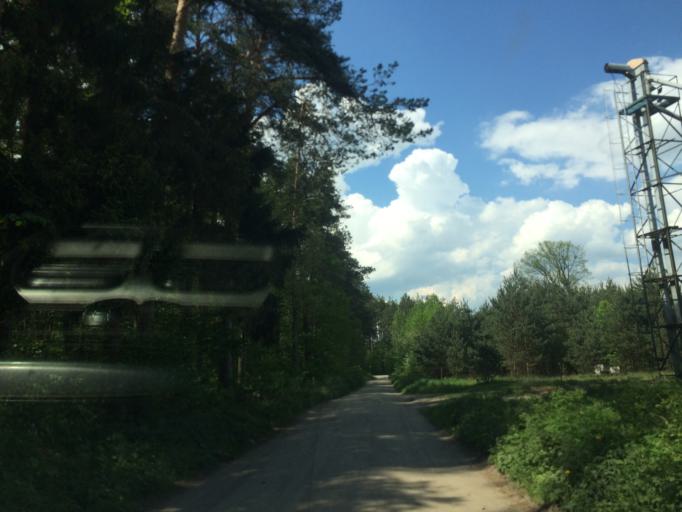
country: PL
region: Warmian-Masurian Voivodeship
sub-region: Powiat nowomiejski
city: Nowe Miasto Lubawskie
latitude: 53.4530
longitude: 19.6139
